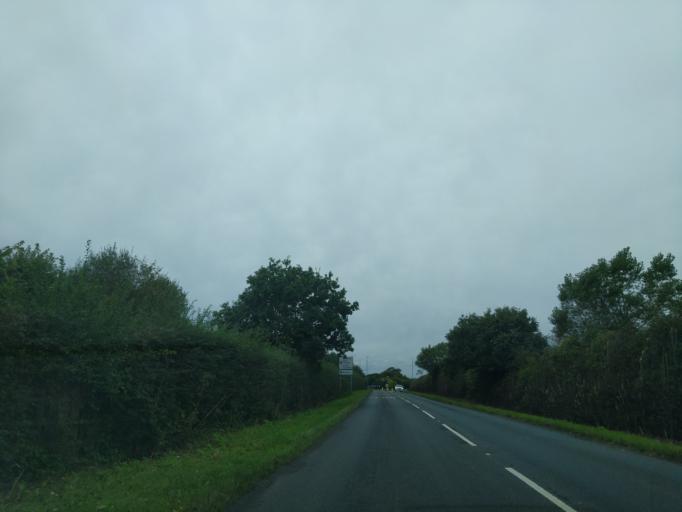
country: GB
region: England
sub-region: Cheshire East
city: Weston
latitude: 53.0560
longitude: -2.3880
